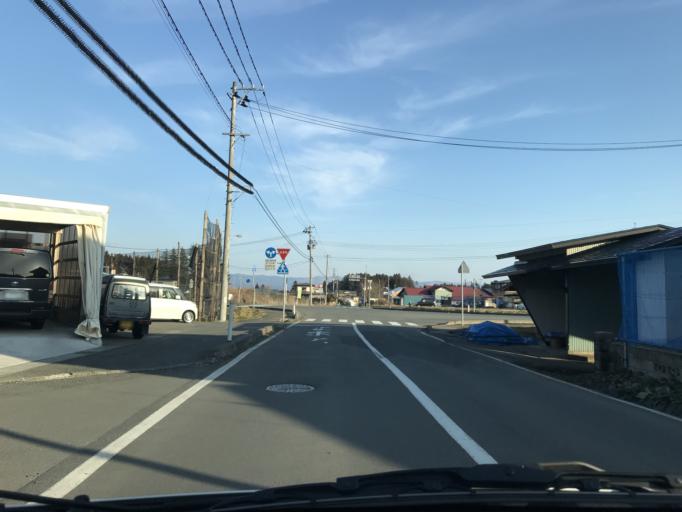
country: JP
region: Iwate
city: Kitakami
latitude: 39.2195
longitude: 141.1079
